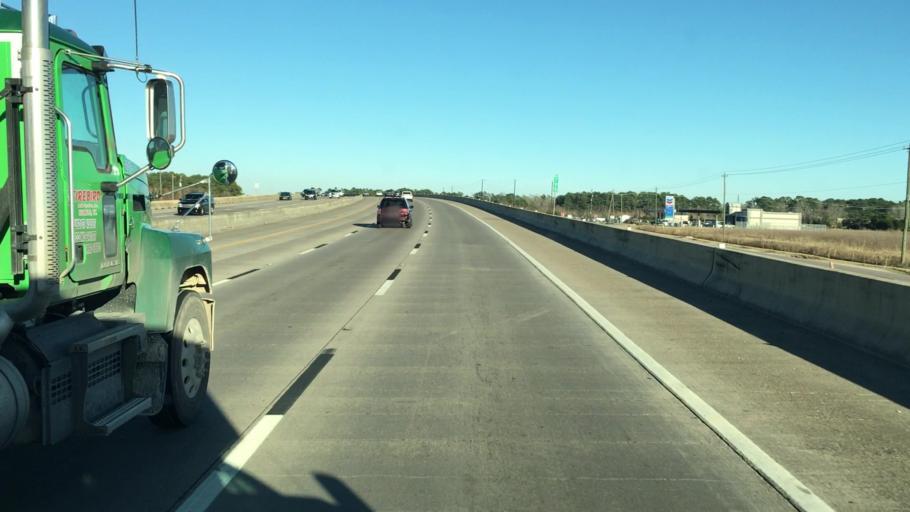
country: US
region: Texas
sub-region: Chambers County
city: Mont Belvieu
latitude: 29.8114
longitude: -94.9422
